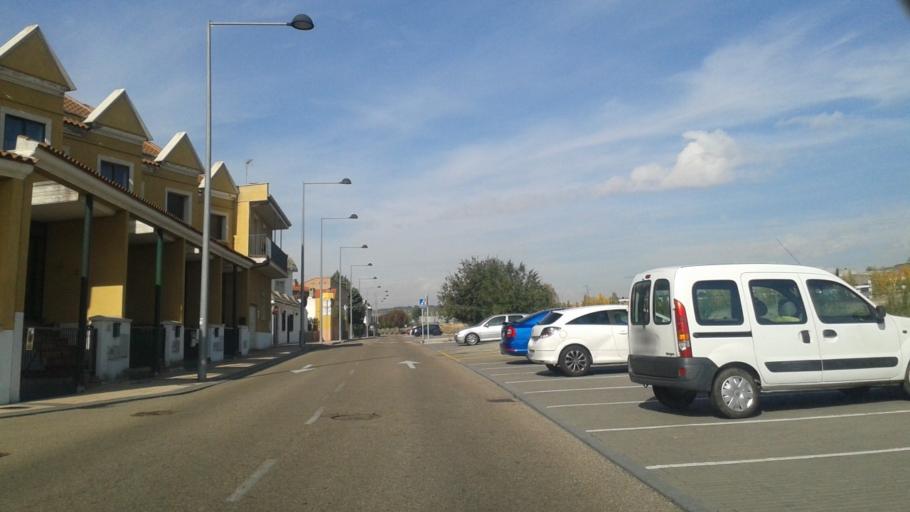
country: ES
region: Castille and Leon
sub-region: Provincia de Valladolid
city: Arroyo
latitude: 41.6295
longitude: -4.7714
